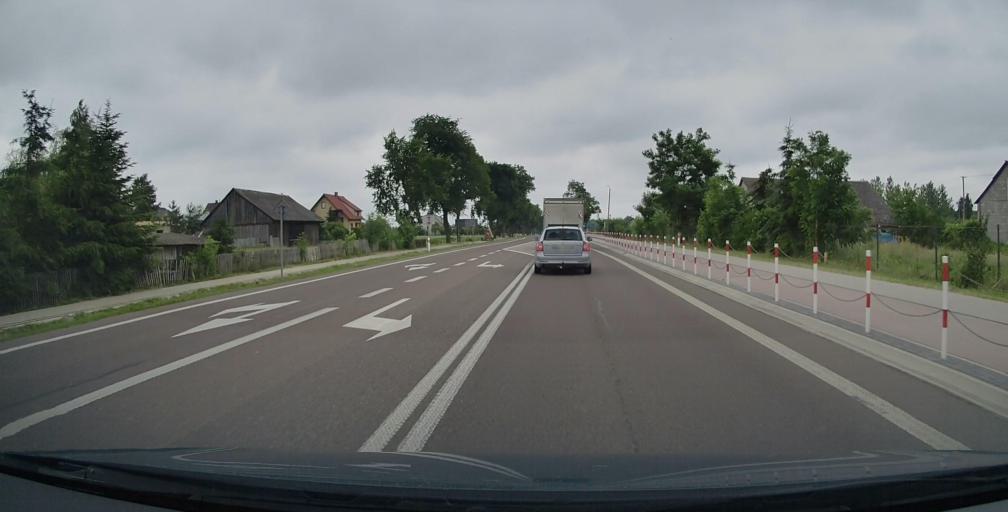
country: PL
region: Lublin Voivodeship
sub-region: Powiat bialski
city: Rzeczyca
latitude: 52.0190
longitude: 22.7259
